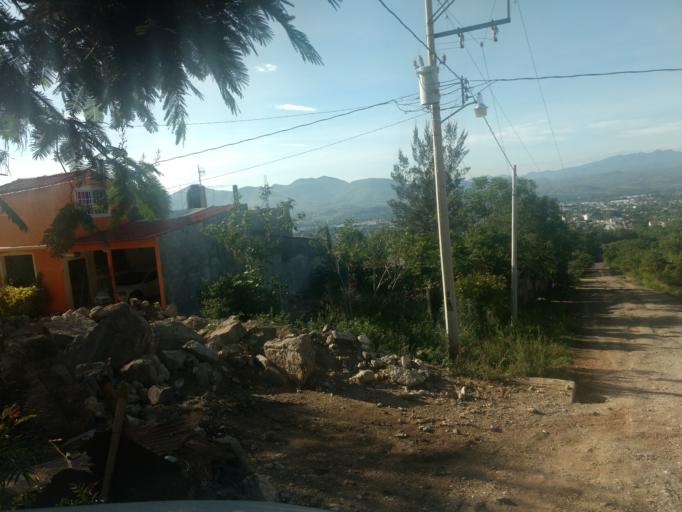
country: MX
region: Oaxaca
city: Ciudad de Huajuapam de Leon
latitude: 17.8271
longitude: -97.7944
